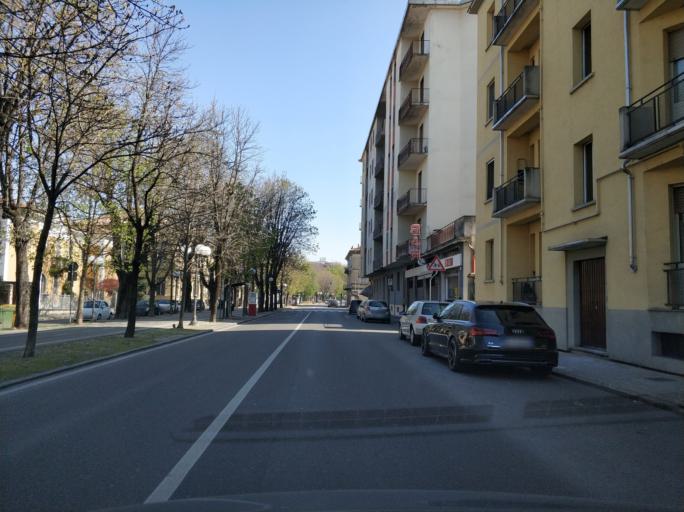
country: IT
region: Piedmont
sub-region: Provincia di Vercelli
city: Vercelli
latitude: 45.3284
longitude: 8.4267
